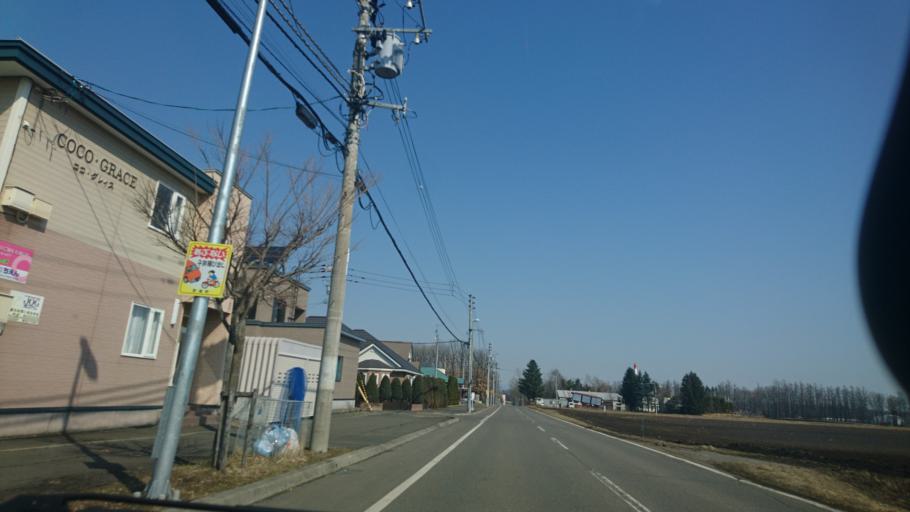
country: JP
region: Hokkaido
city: Obihiro
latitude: 42.9138
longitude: 143.0767
